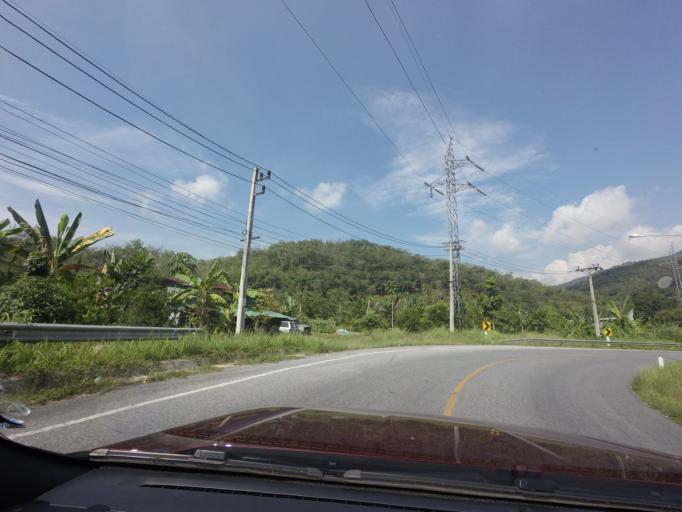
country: TH
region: Yala
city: Betong
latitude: 5.8721
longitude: 101.1331
